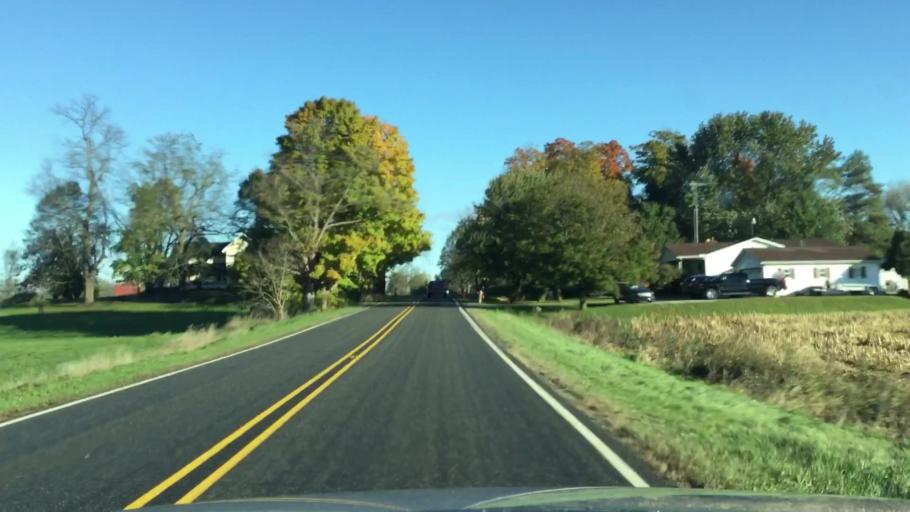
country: US
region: Michigan
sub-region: Shiawassee County
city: Durand
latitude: 42.8376
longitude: -83.9451
